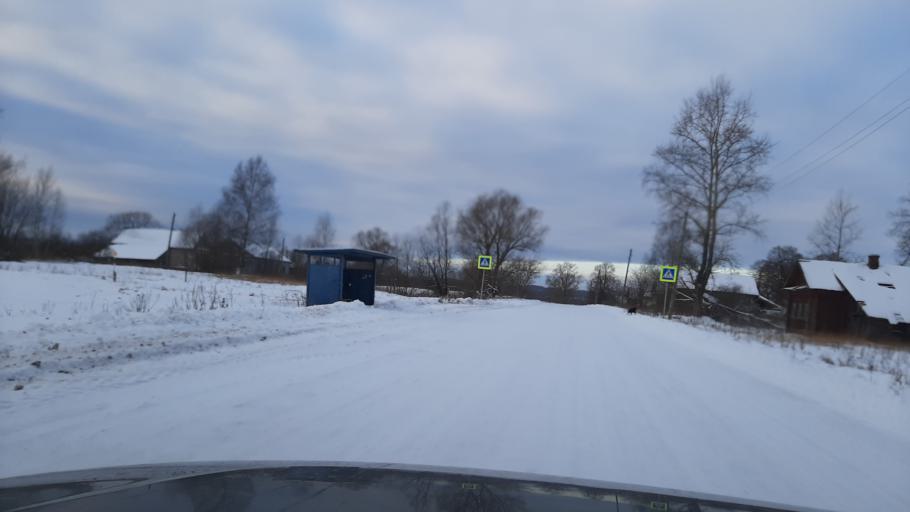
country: RU
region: Kostroma
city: Kosmynino
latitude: 57.4840
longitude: 40.8115
